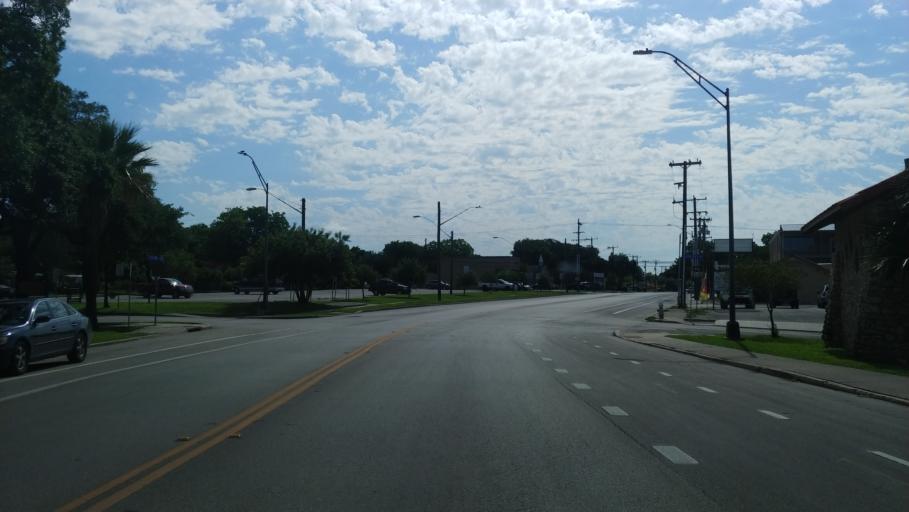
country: US
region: Texas
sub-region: Bexar County
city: San Antonio
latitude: 29.4498
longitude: -98.5283
